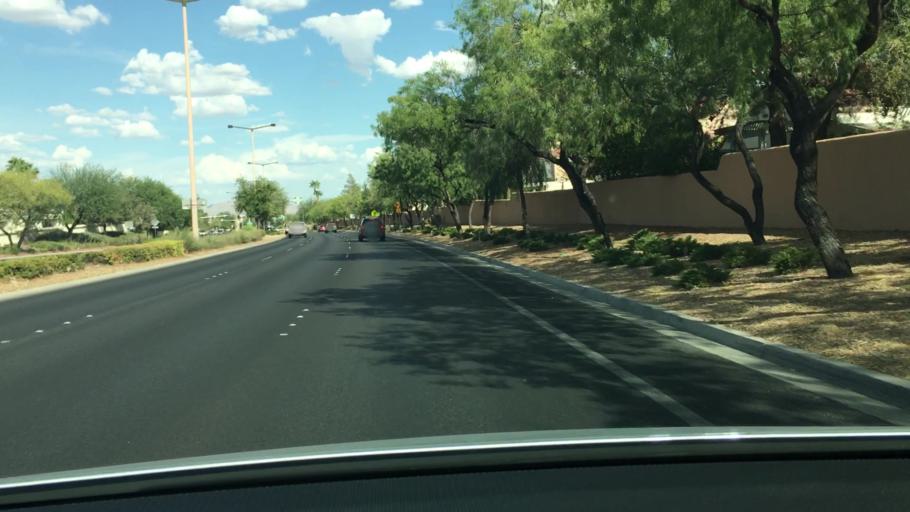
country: US
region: Nevada
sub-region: Clark County
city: Spring Valley
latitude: 36.1967
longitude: -115.2737
